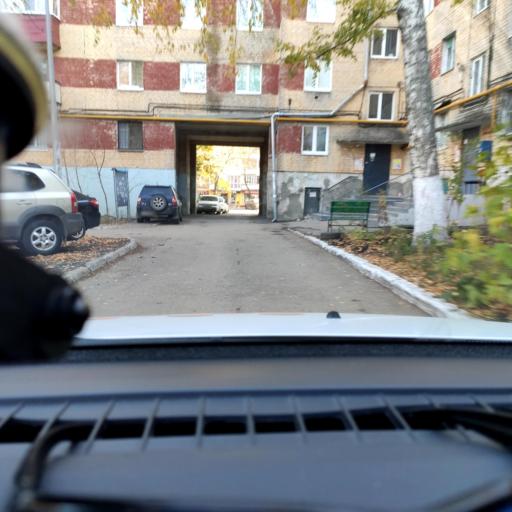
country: RU
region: Samara
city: Samara
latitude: 53.2114
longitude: 50.1696
